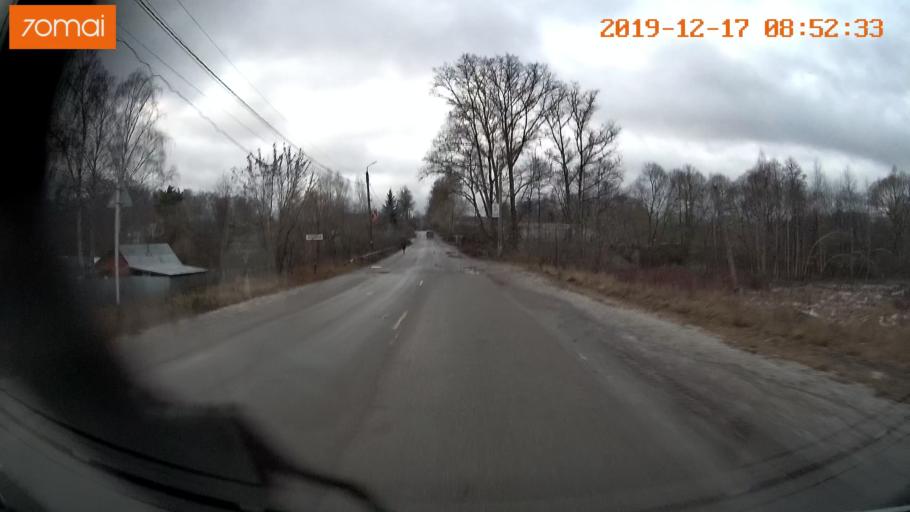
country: RU
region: Vladimir
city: Kosterevo
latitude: 55.9477
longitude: 39.6325
